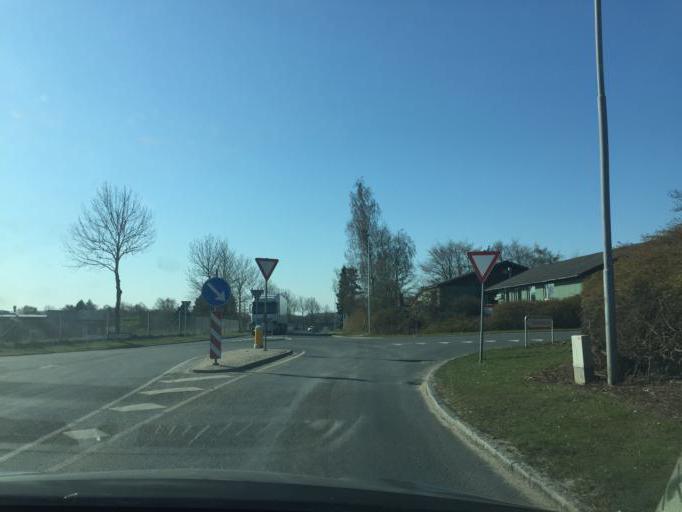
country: DK
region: South Denmark
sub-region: Faaborg-Midtfyn Kommune
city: Ringe
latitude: 55.2490
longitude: 10.4858
